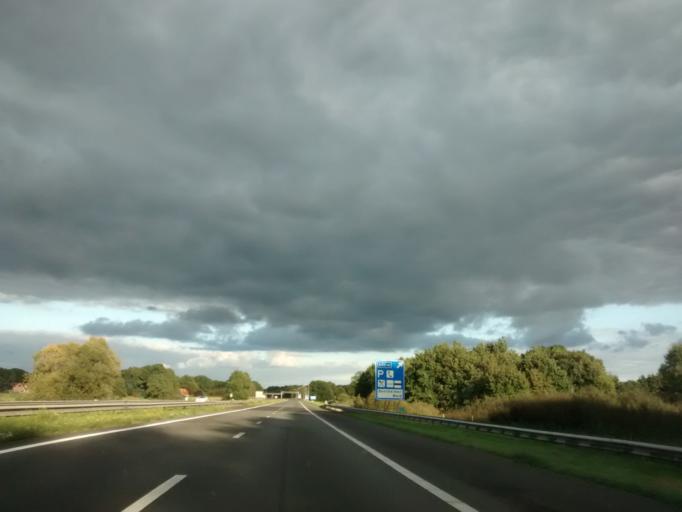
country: NL
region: Overijssel
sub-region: Gemeente Losser
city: Losser
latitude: 52.3112
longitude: 7.0209
